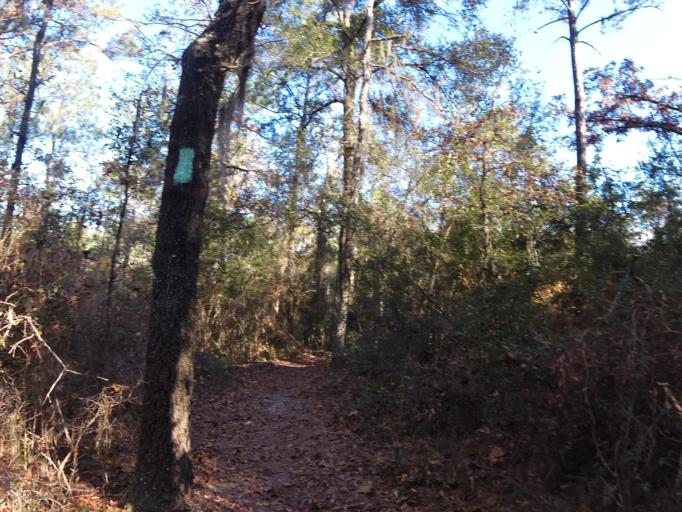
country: US
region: Florida
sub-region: Clay County
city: Middleburg
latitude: 30.1523
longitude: -81.9624
